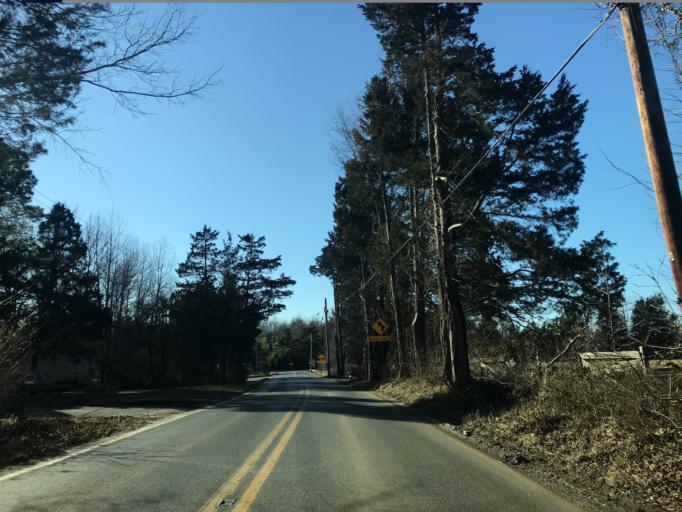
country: US
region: Maryland
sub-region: Prince George's County
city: Accokeek
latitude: 38.6697
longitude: -76.9901
